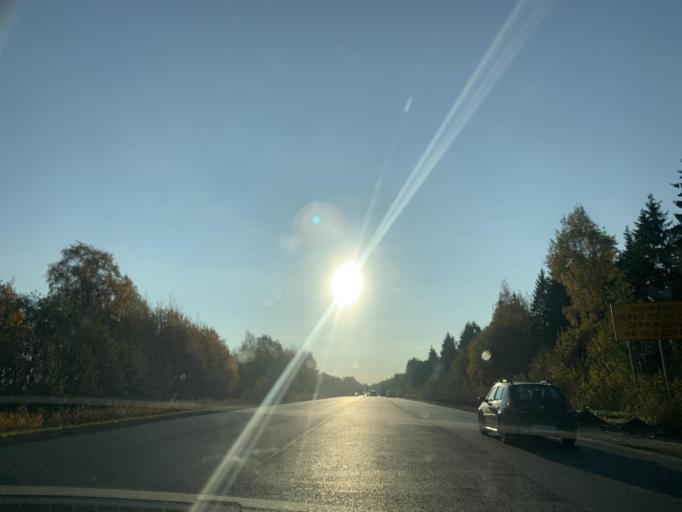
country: RU
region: Jaroslavl
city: Konstantinovskiy
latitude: 57.7859
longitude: 39.6163
